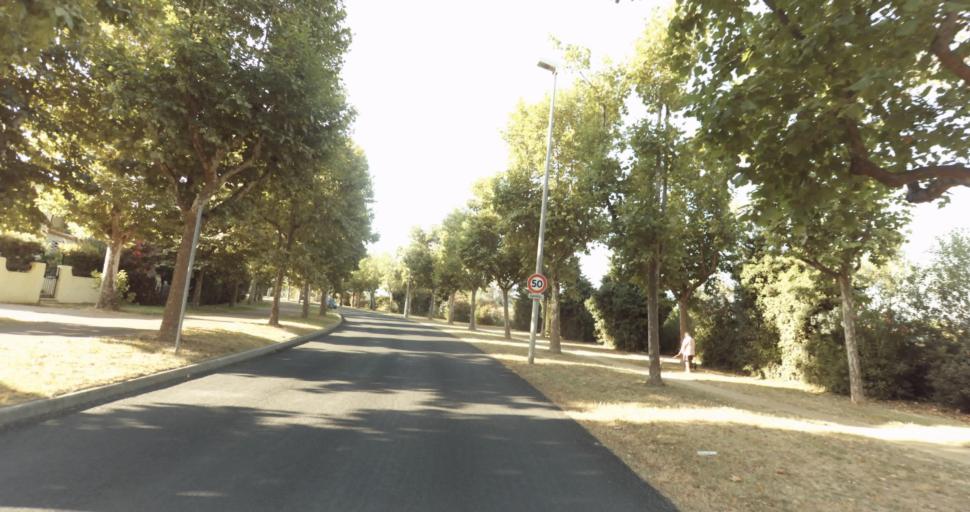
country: FR
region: Languedoc-Roussillon
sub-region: Departement des Pyrenees-Orientales
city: Saint-Cyprien-Plage
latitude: 42.6018
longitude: 3.0354
